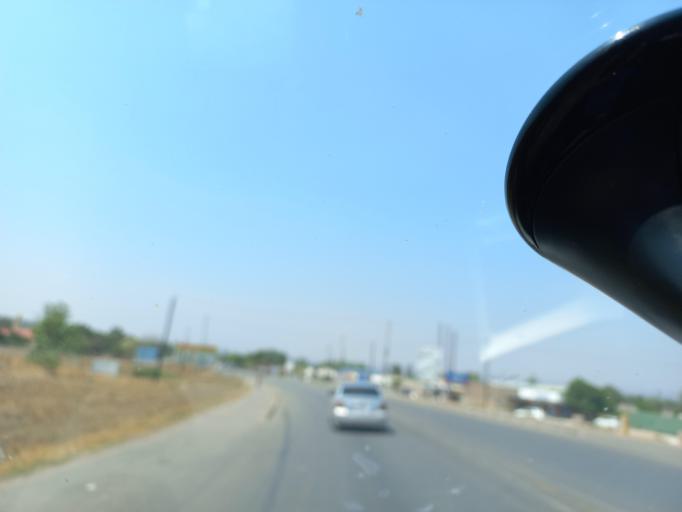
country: ZM
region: Lusaka
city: Kafue
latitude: -15.7608
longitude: 28.1786
